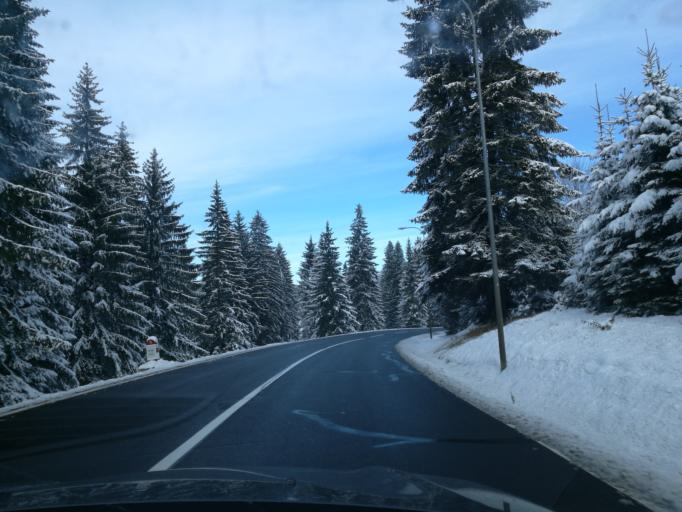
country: RO
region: Brasov
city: Brasov
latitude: 45.6054
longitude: 25.5543
